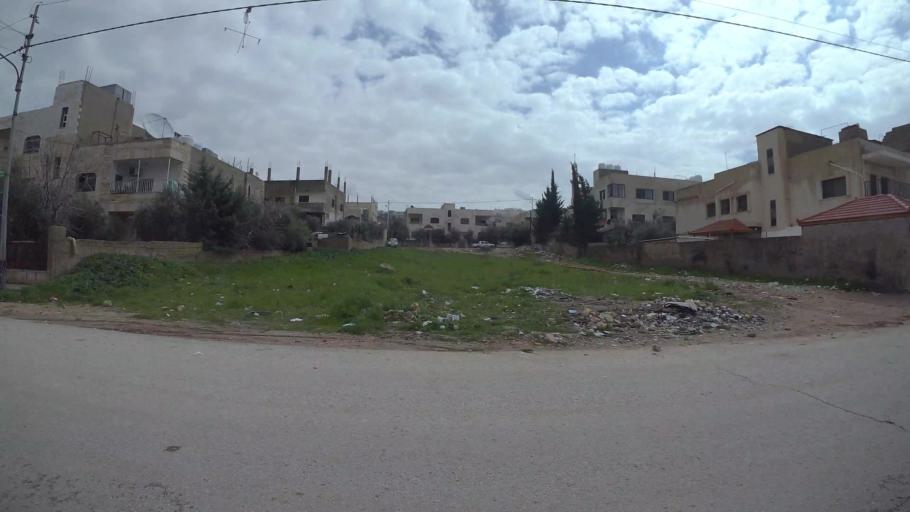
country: JO
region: Amman
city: Al Jubayhah
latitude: 32.0502
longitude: 35.8270
